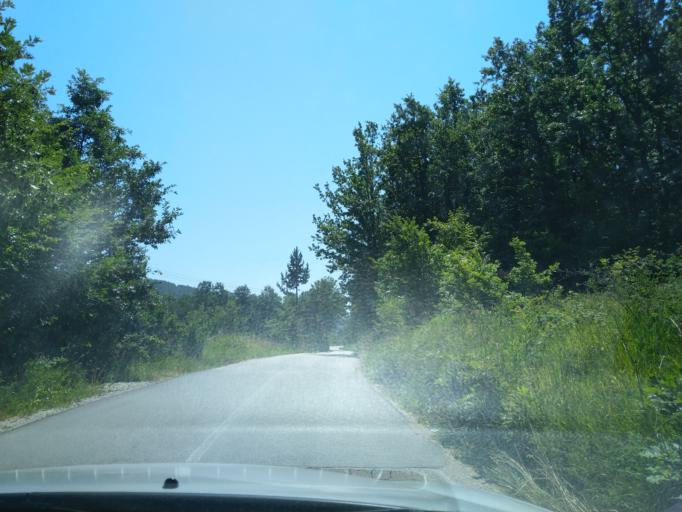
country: RS
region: Central Serbia
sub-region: Zlatiborski Okrug
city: Uzice
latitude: 43.7838
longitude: 19.8557
